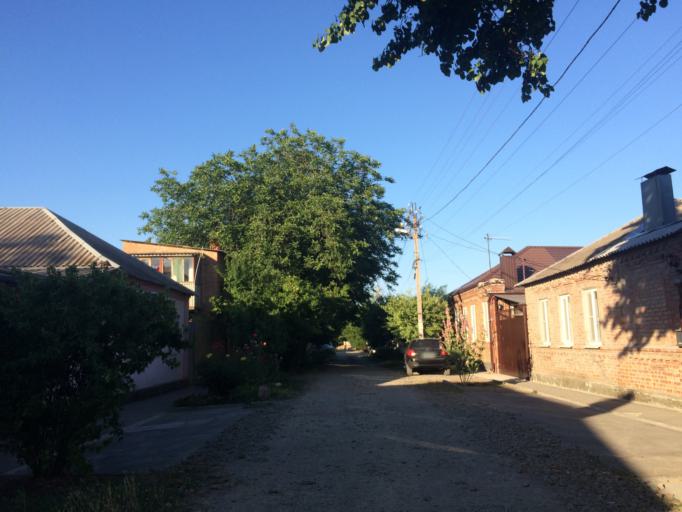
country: RU
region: Rostov
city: Rostov-na-Donu
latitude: 47.2172
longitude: 39.6436
